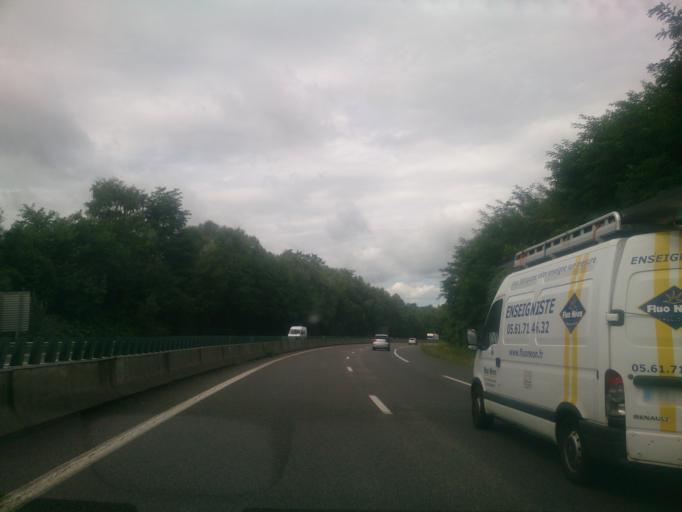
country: FR
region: Midi-Pyrenees
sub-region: Departement des Hautes-Pyrenees
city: Capvern
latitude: 43.1071
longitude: 0.3270
